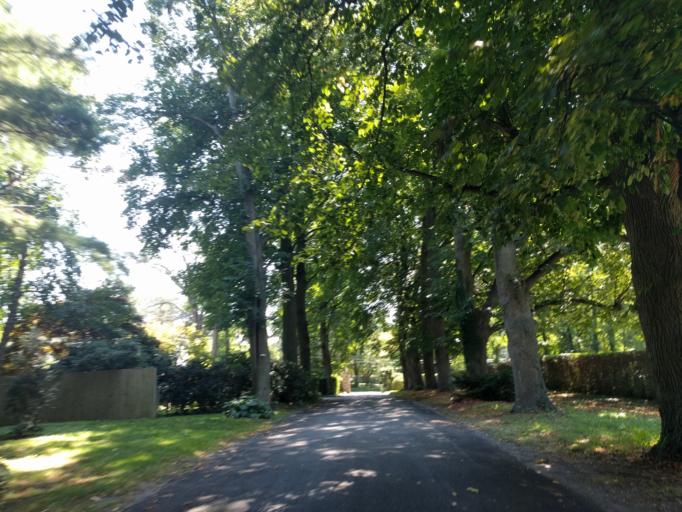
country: US
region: New York
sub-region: Nassau County
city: Locust Valley
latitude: 40.8829
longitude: -73.5975
